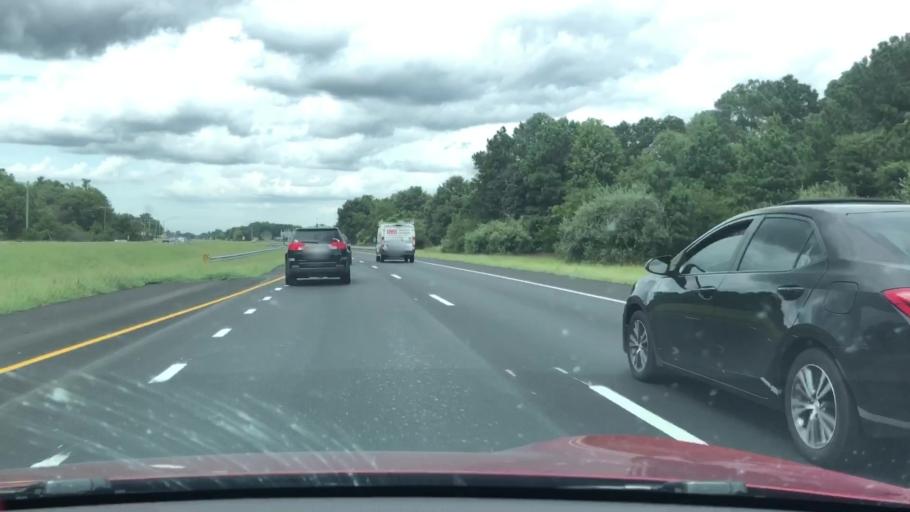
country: US
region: Maryland
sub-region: Somerset County
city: Princess Anne
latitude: 38.1637
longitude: -75.6890
